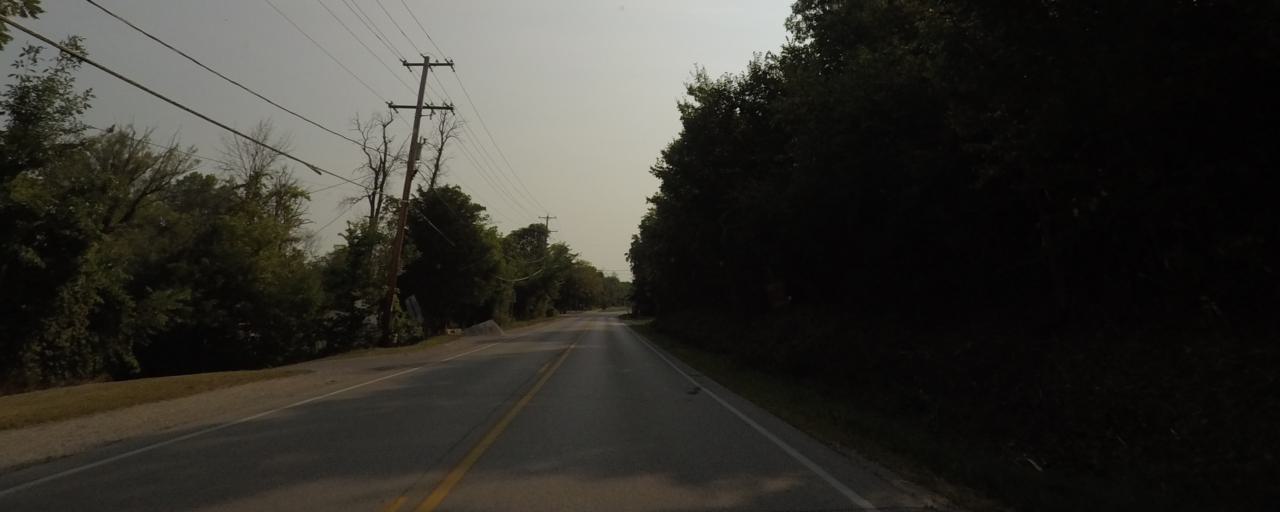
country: US
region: Wisconsin
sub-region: Waukesha County
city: Delafield
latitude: 43.0582
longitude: -88.4248
